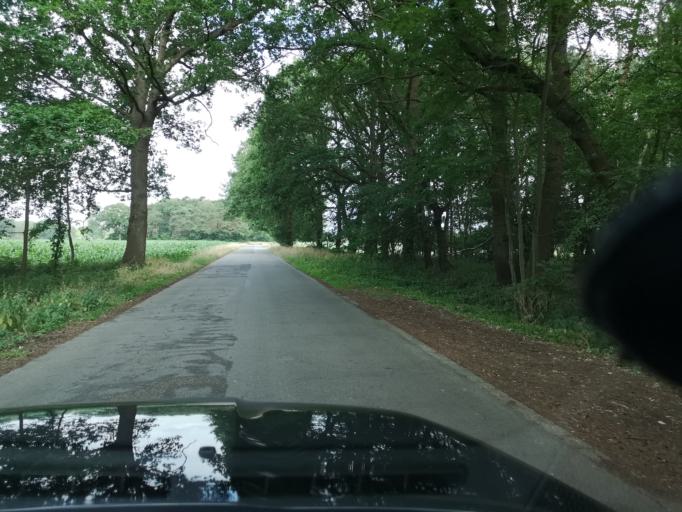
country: DE
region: North Rhine-Westphalia
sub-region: Regierungsbezirk Dusseldorf
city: Wesel
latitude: 51.7095
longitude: 6.6304
